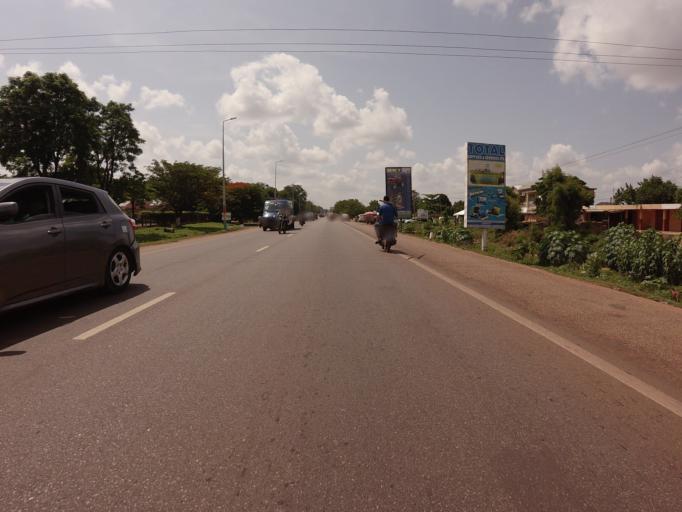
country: GH
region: Northern
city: Tamale
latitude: 9.4437
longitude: -0.8442
